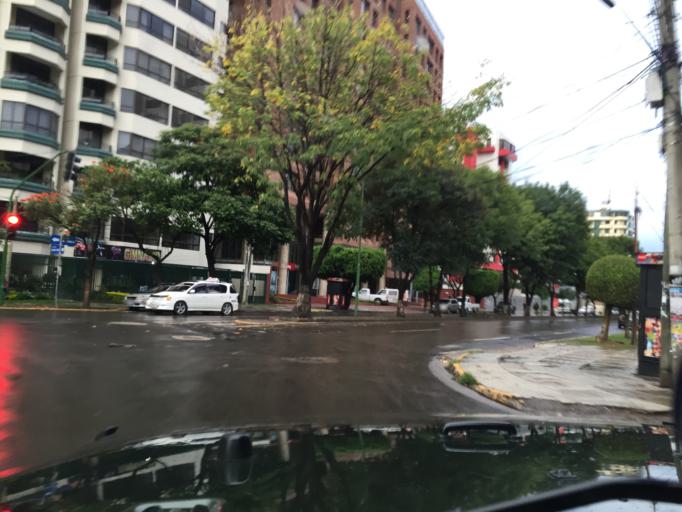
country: BO
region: Cochabamba
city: Cochabamba
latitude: -17.3727
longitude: -66.1571
